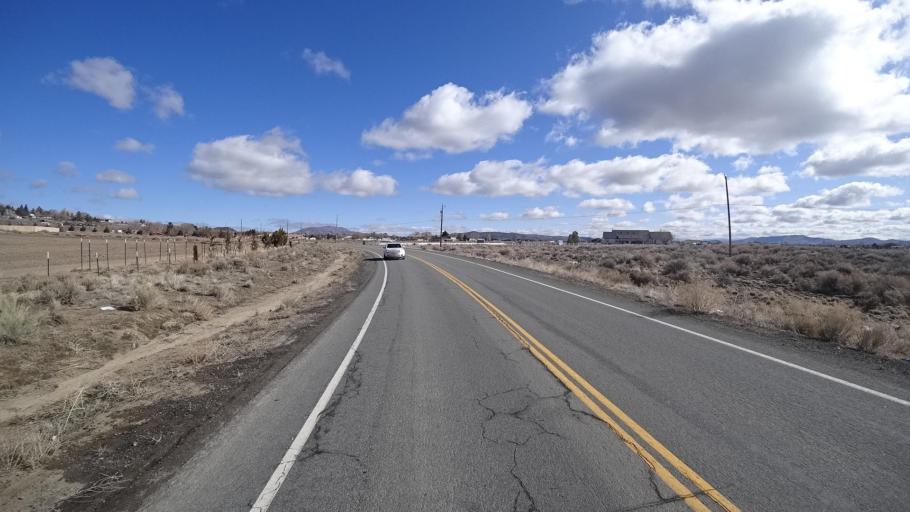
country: US
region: Nevada
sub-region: Washoe County
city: Cold Springs
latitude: 39.6530
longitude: -119.9231
